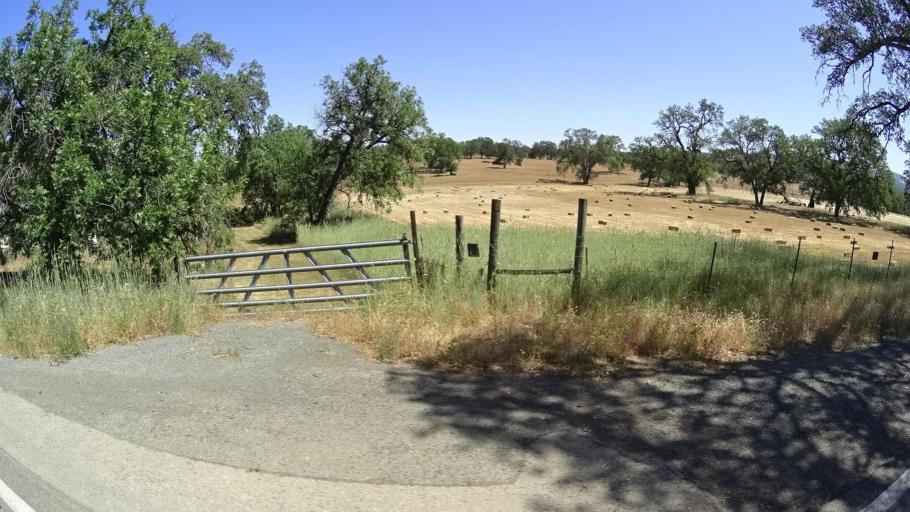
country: US
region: California
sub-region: Lake County
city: Lower Lake
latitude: 38.9097
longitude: -122.6023
